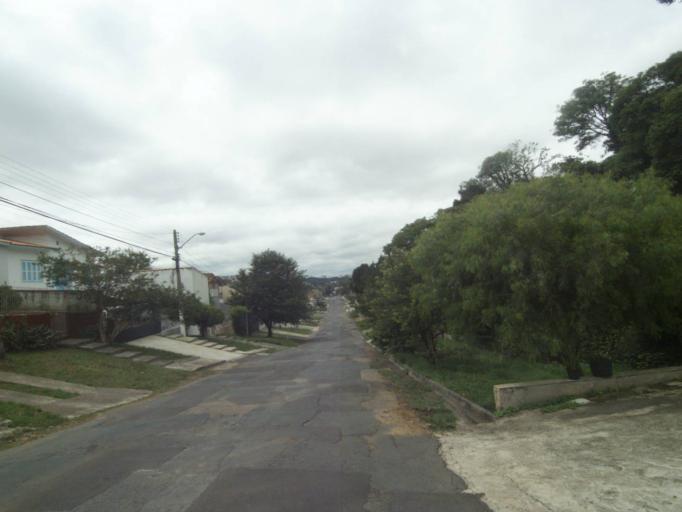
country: BR
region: Parana
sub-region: Curitiba
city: Curitiba
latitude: -25.3894
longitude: -49.2761
